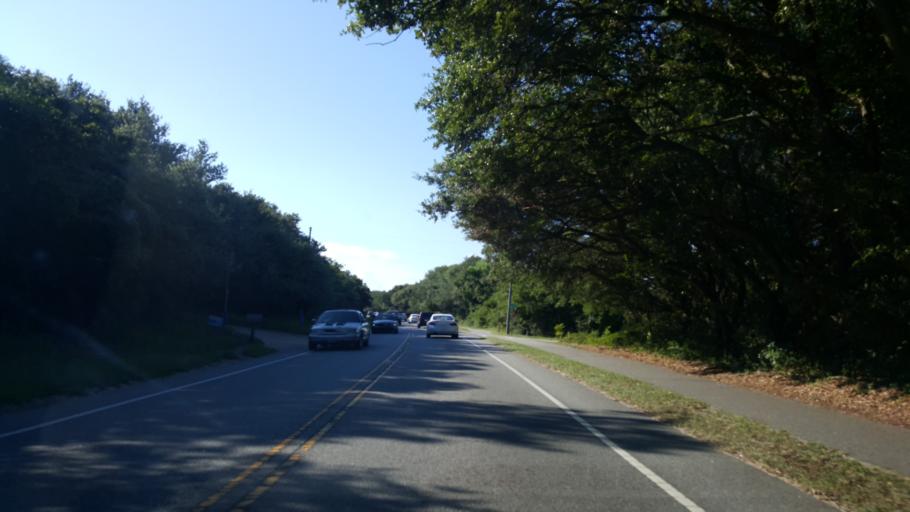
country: US
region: North Carolina
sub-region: Dare County
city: Southern Shores
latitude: 36.1401
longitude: -75.7369
